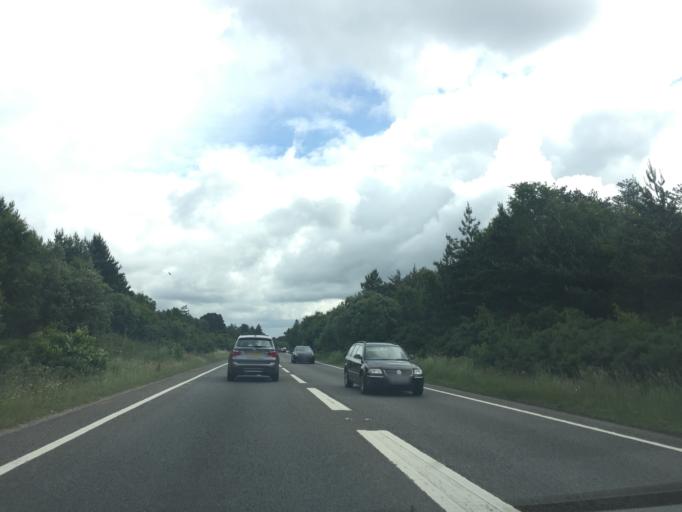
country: GB
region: England
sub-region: Dorset
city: Ferndown
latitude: 50.8104
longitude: -1.9286
